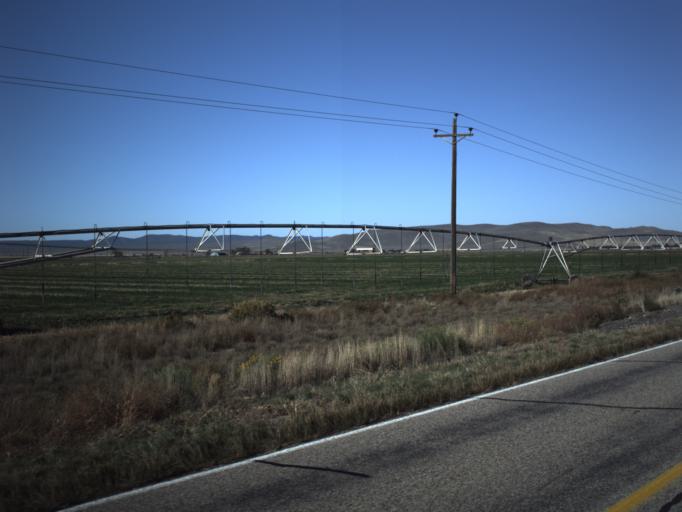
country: US
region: Utah
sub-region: Washington County
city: Enterprise
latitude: 37.7117
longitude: -113.6624
